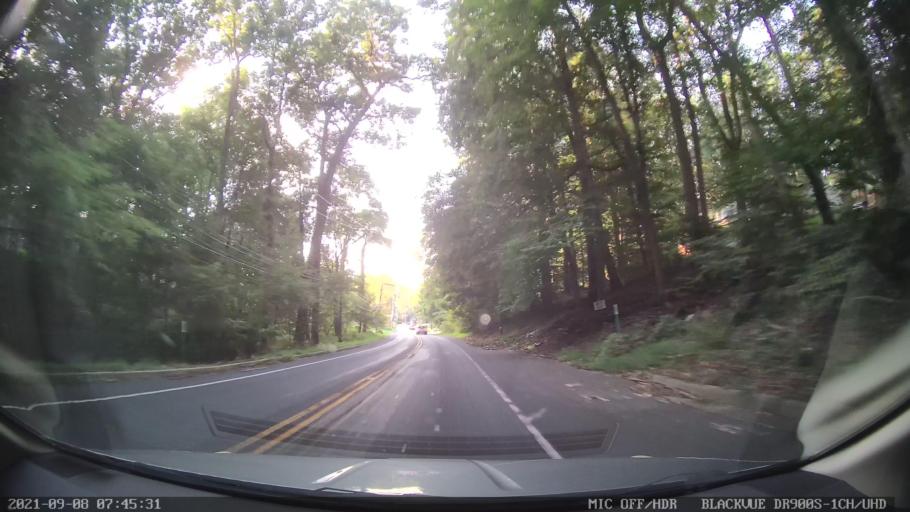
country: US
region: Pennsylvania
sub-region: Delaware County
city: Radnor
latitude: 40.0565
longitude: -75.3676
